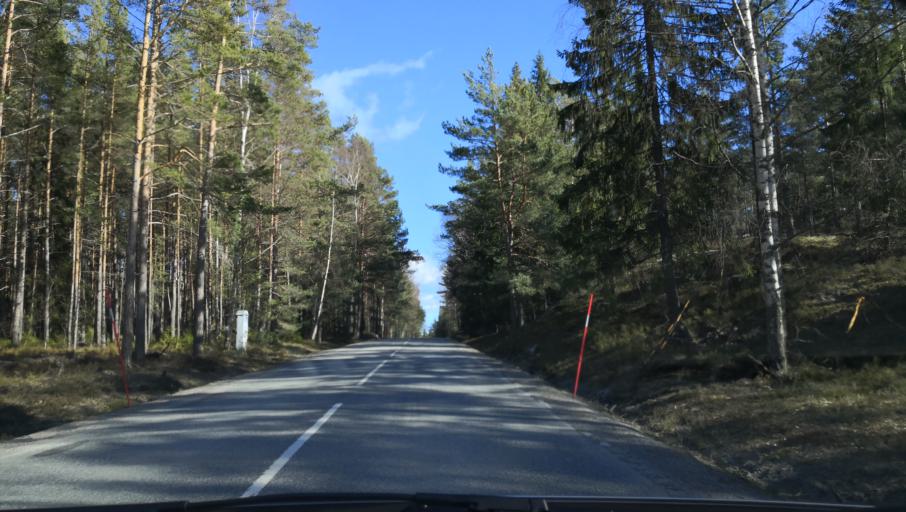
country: SE
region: Stockholm
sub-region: Varmdo Kommun
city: Hemmesta
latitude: 59.3568
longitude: 18.5921
